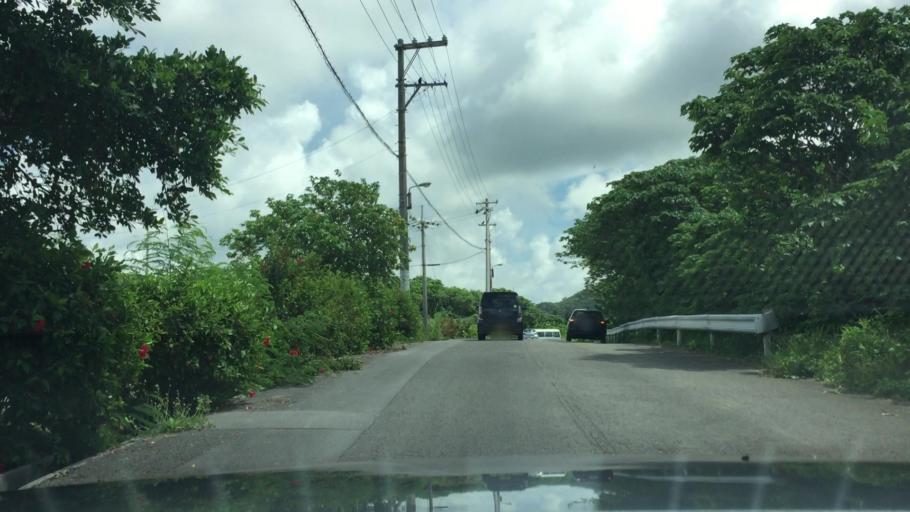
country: JP
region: Okinawa
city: Ishigaki
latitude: 24.3604
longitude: 124.1545
